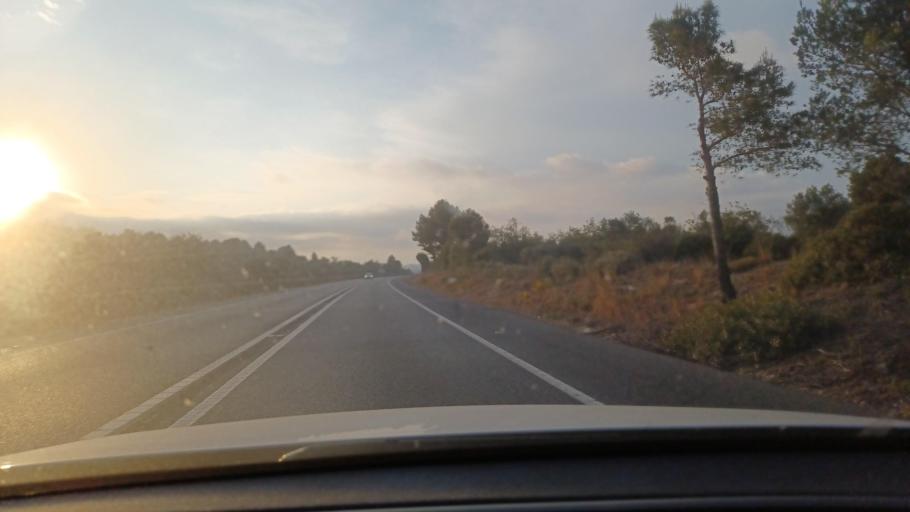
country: ES
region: Catalonia
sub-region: Provincia de Tarragona
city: l'Ametlla de Mar
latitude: 40.8951
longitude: 0.7594
